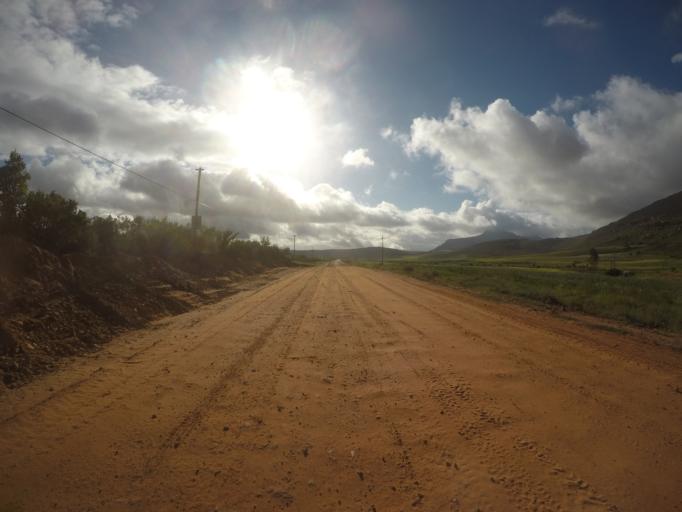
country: ZA
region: Western Cape
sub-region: West Coast District Municipality
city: Clanwilliam
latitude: -32.3433
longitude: 18.8221
